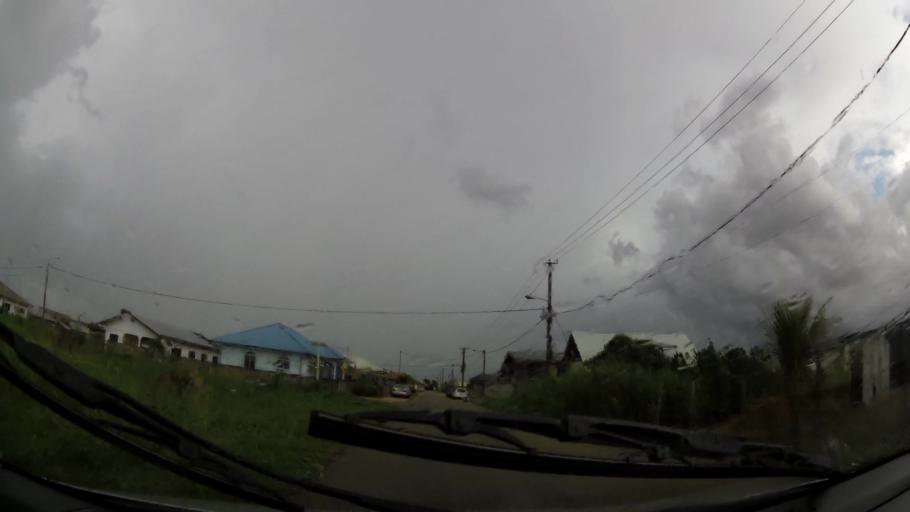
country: SR
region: Commewijne
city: Nieuw Amsterdam
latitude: 5.8516
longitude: -55.1143
